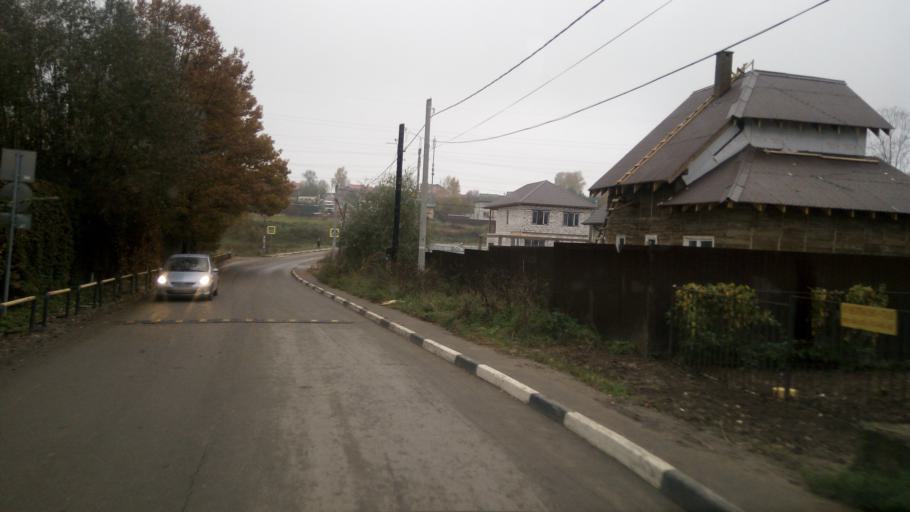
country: RU
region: Moskovskaya
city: Skhodnya
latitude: 55.9367
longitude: 37.2886
